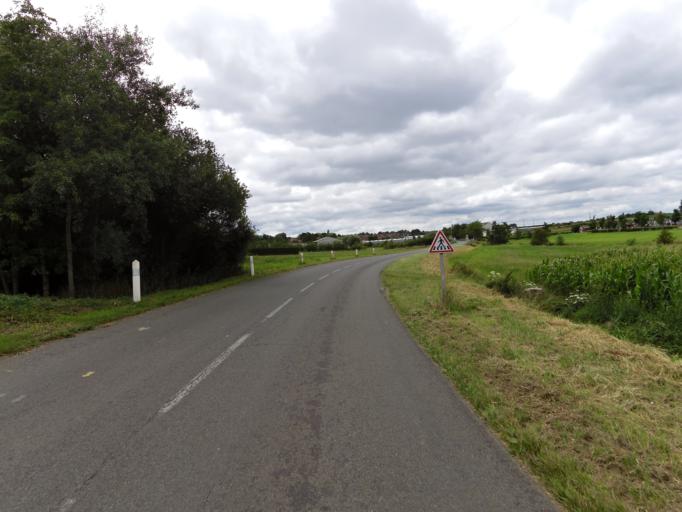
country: FR
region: Nord-Pas-de-Calais
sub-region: Departement du Nord
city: Godewaersvelde
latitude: 50.7984
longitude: 2.6517
